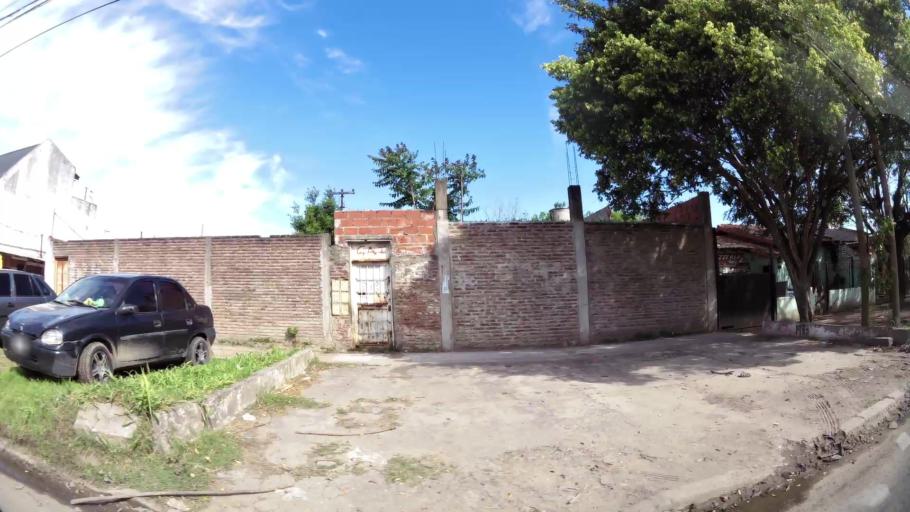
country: AR
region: Buenos Aires
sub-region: Partido de Quilmes
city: Quilmes
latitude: -34.7669
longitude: -58.3127
